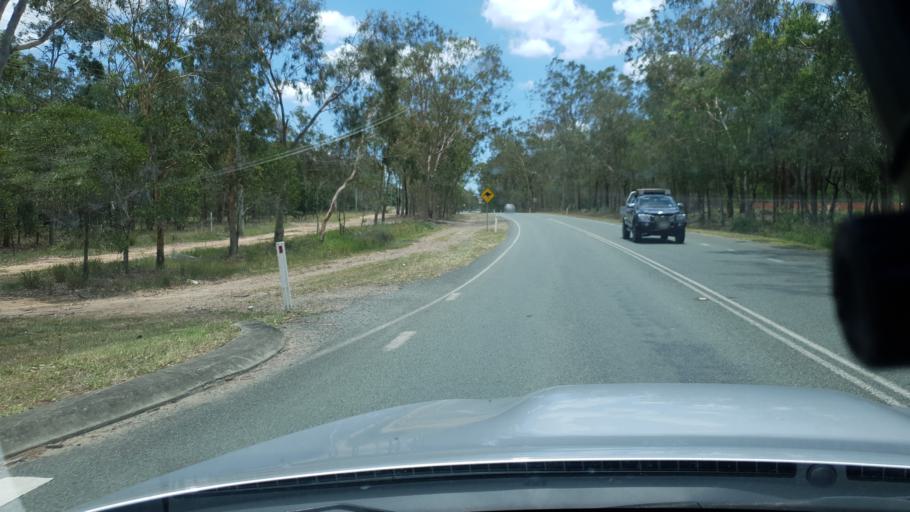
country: AU
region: Queensland
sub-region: Logan
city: North Maclean
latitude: -27.7339
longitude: 152.9849
